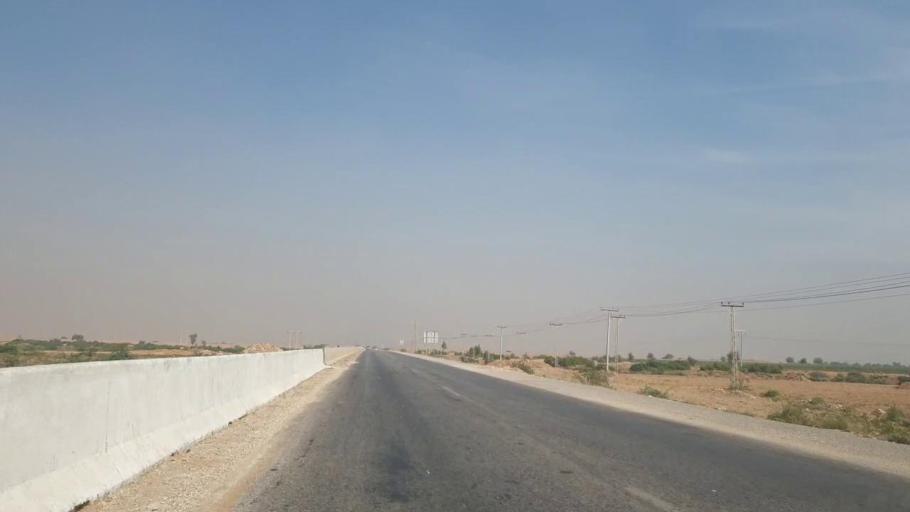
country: PK
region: Sindh
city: Jamshoro
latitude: 25.5227
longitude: 68.2755
